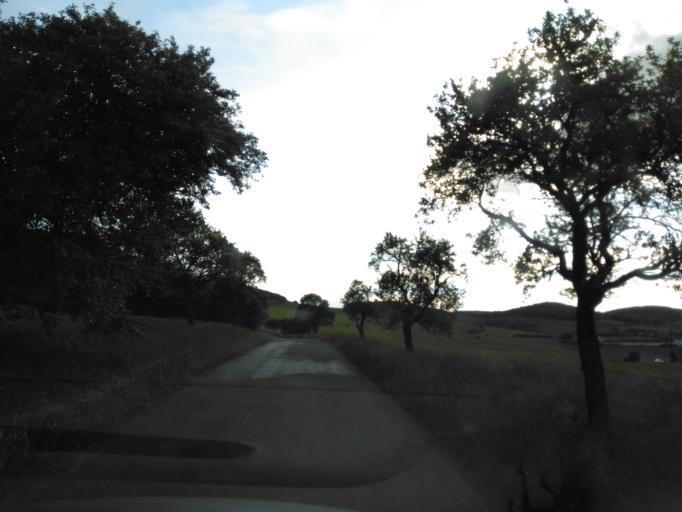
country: CZ
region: Central Bohemia
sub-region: Okres Beroun
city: Beroun
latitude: 49.9049
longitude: 14.1268
